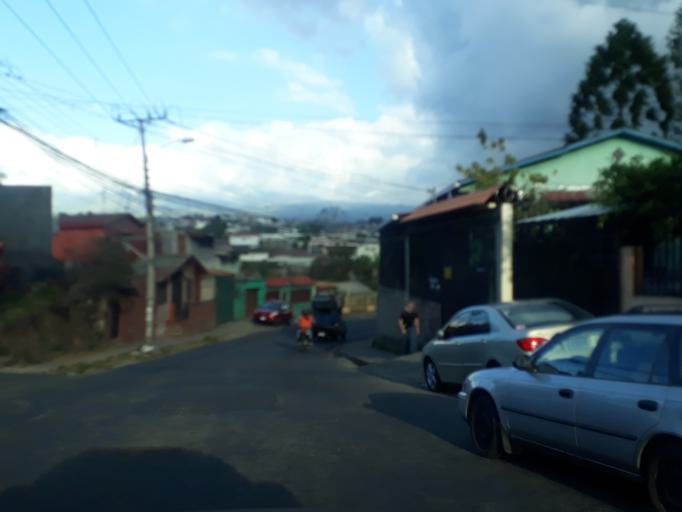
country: CR
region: San Jose
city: Purral
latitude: 9.9569
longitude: -84.0376
